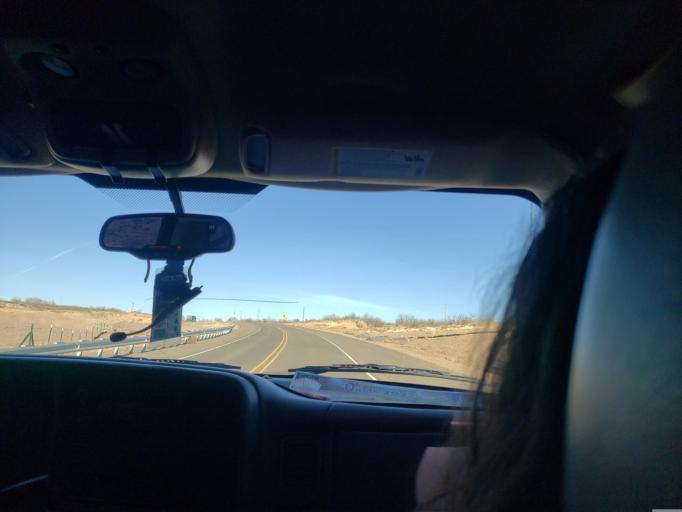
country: US
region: New Mexico
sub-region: Quay County
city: Logan
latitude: 35.3560
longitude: -103.4123
